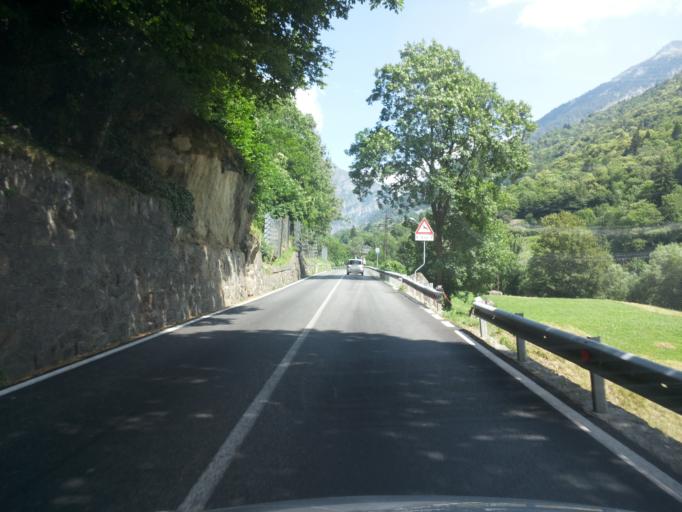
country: IT
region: Aosta Valley
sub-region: Valle d'Aosta
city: Fontainemore
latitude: 45.6551
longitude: 7.8598
